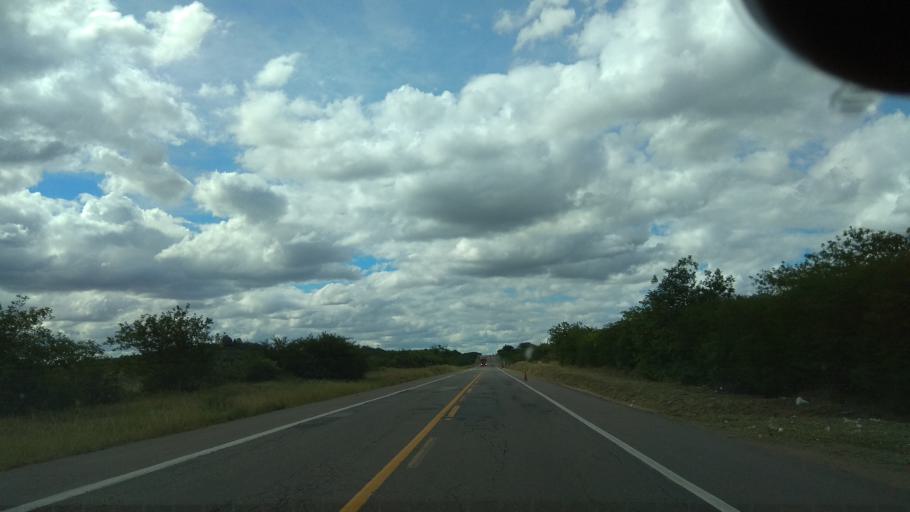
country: BR
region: Bahia
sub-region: Santa Ines
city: Santa Ines
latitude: -12.9805
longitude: -39.9403
